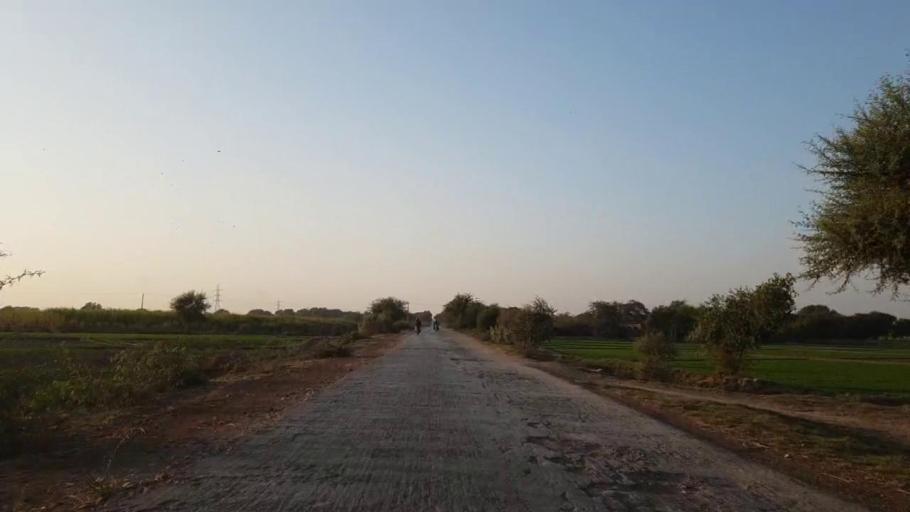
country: PK
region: Sindh
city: Chambar
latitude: 25.2317
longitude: 68.7047
